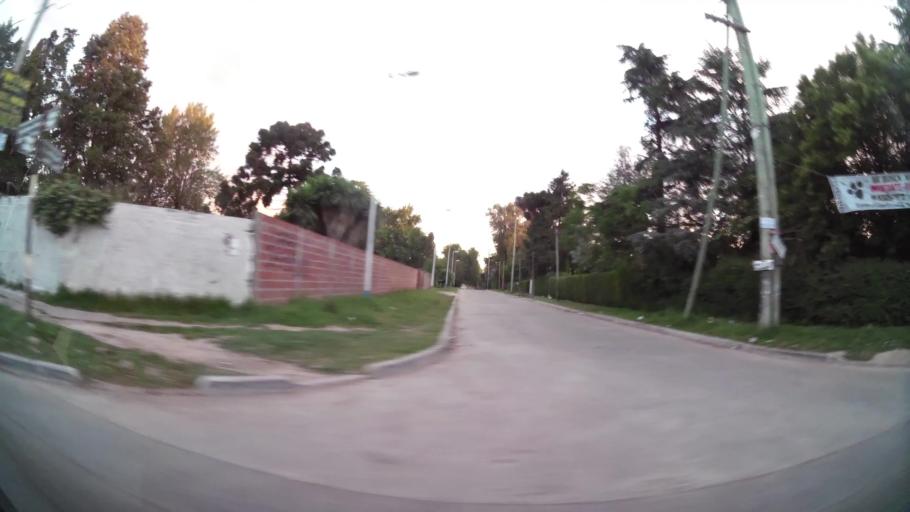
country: AR
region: Buenos Aires
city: Santa Catalina - Dique Lujan
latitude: -34.4798
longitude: -58.7724
